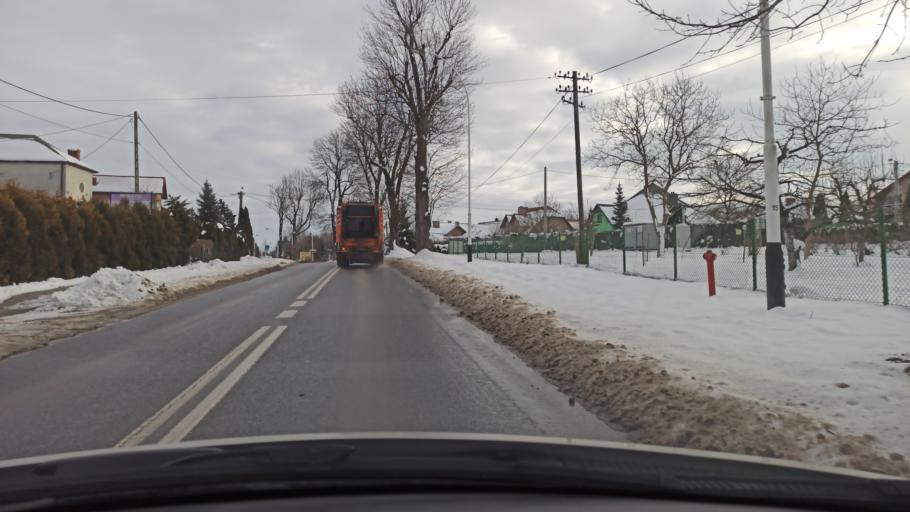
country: PL
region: Subcarpathian Voivodeship
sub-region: Powiat lezajski
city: Lezajsk
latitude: 50.2517
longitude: 22.4279
